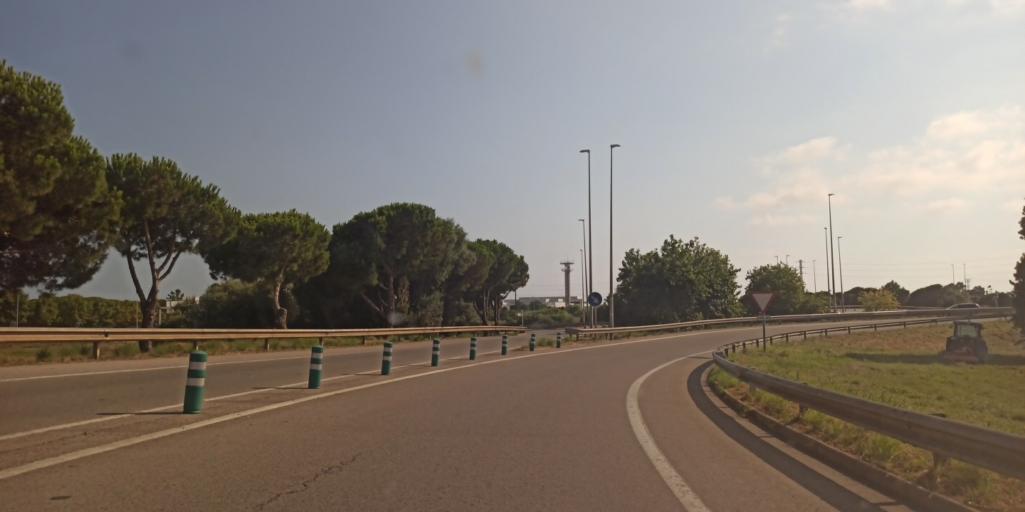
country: ES
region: Catalonia
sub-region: Provincia de Barcelona
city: Gava
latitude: 41.2921
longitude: 2.0110
